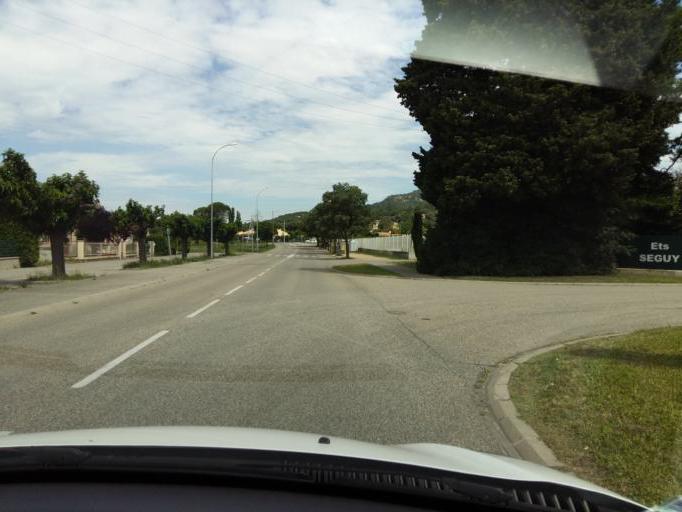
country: FR
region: Provence-Alpes-Cote d'Azur
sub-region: Departement du Vaucluse
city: Bollene
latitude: 44.2988
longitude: 4.7538
